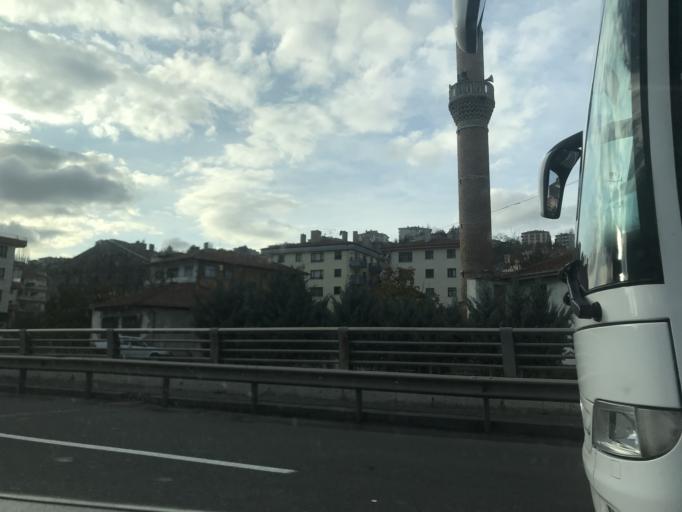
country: TR
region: Ankara
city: Mamak
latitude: 39.9885
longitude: 32.8978
